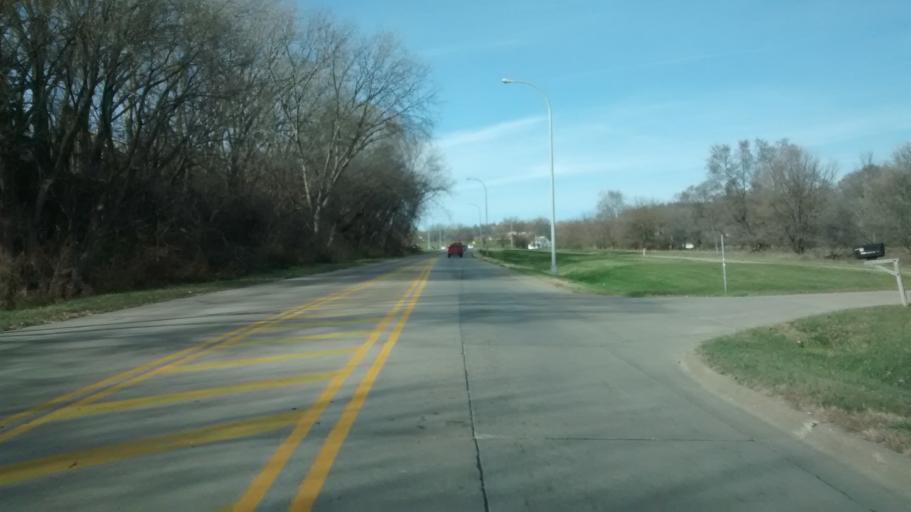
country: US
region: Iowa
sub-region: Woodbury County
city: Sioux City
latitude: 42.5378
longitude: -96.3760
